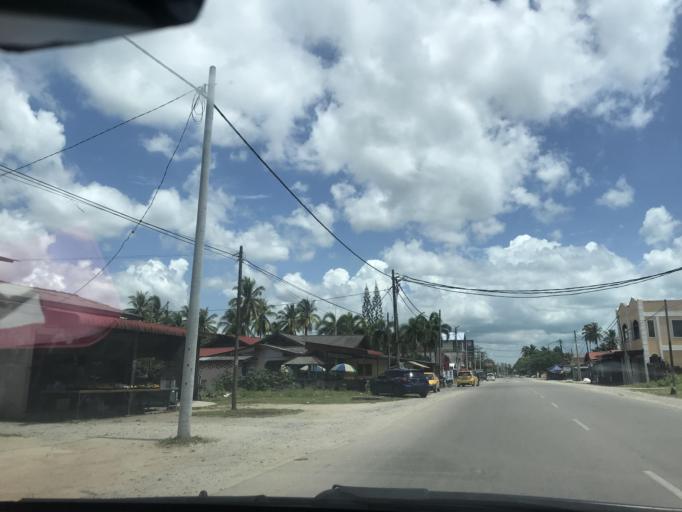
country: TH
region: Narathiwat
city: Tak Bai
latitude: 6.2259
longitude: 102.1030
